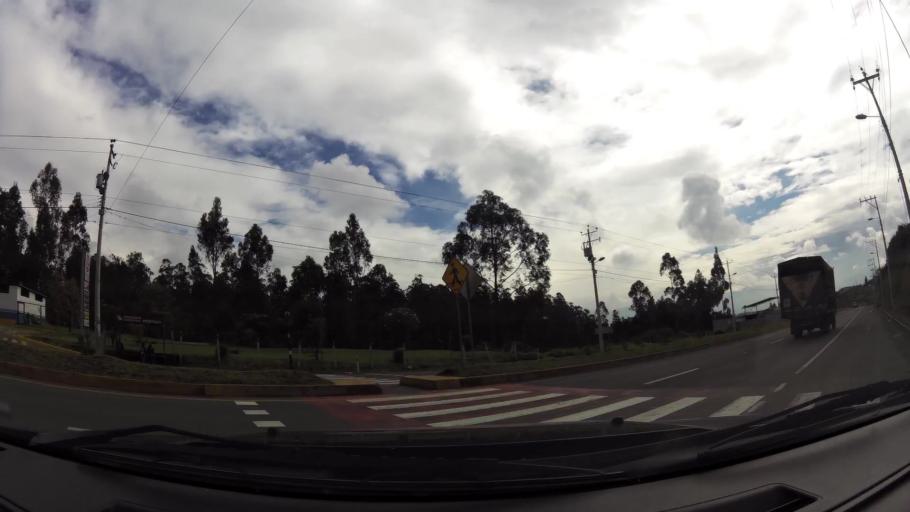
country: EC
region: Pichincha
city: Sangolqui
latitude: -0.3261
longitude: -78.3955
